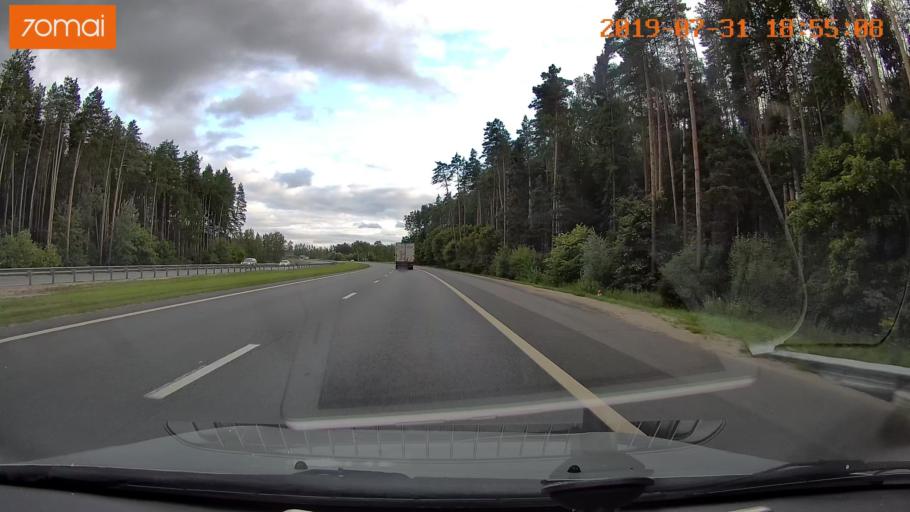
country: RU
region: Moskovskaya
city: Raduzhnyy
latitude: 55.1797
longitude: 38.6678
